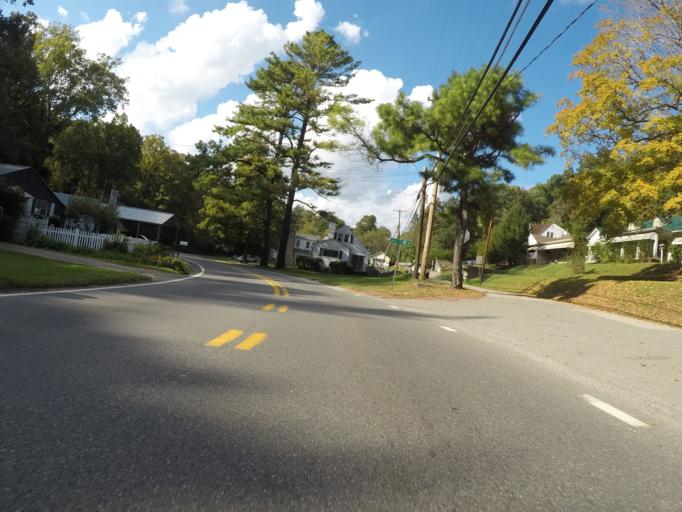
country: US
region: Ohio
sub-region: Lawrence County
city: Burlington
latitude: 38.3878
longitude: -82.5108
